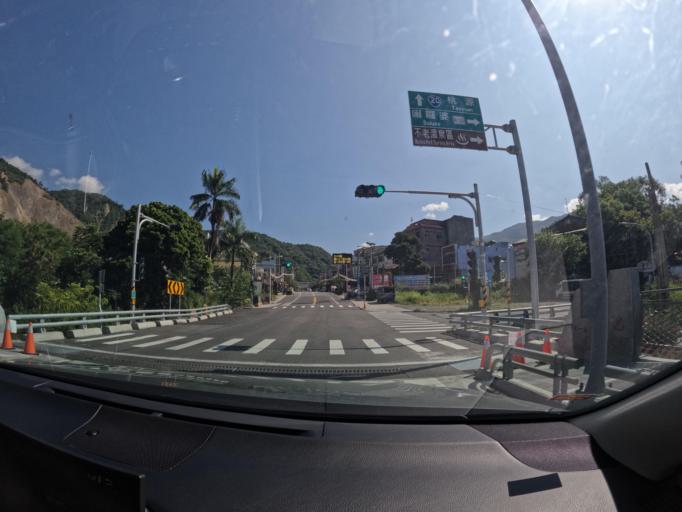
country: TW
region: Taiwan
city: Yujing
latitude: 23.1074
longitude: 120.6980
